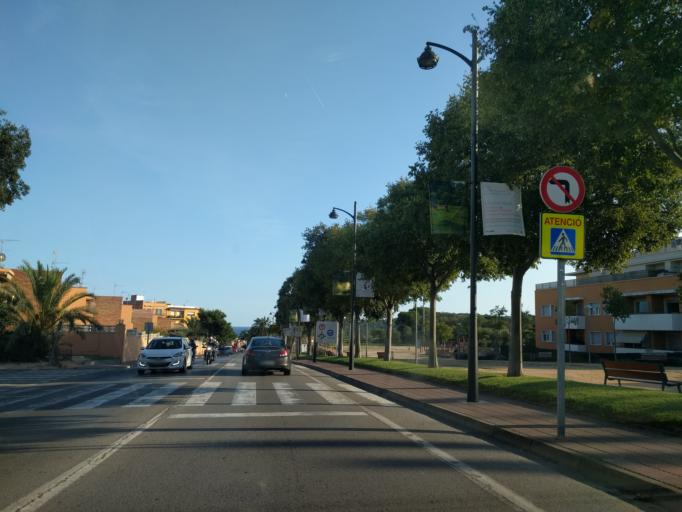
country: ES
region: Catalonia
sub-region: Provincia de Girona
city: Sant Feliu de Guixols
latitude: 41.7918
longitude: 3.0212
